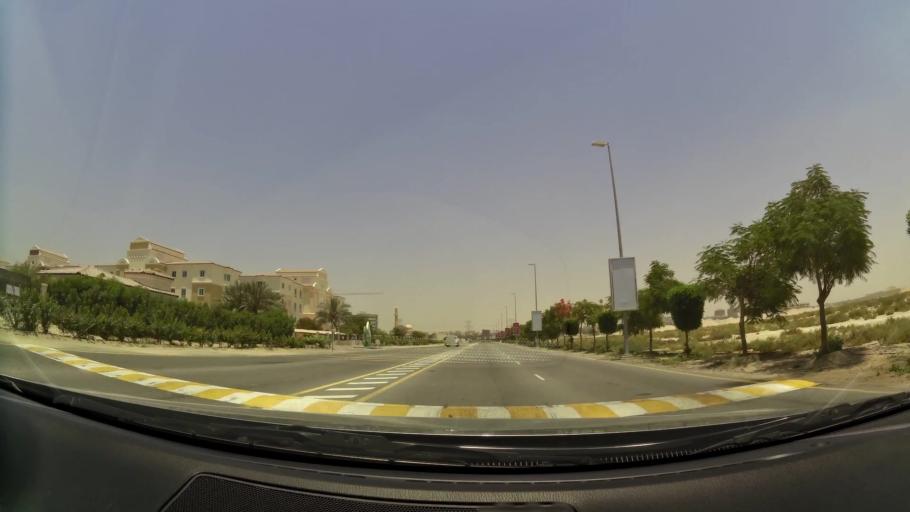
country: AE
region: Dubai
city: Dubai
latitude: 24.9949
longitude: 55.1704
